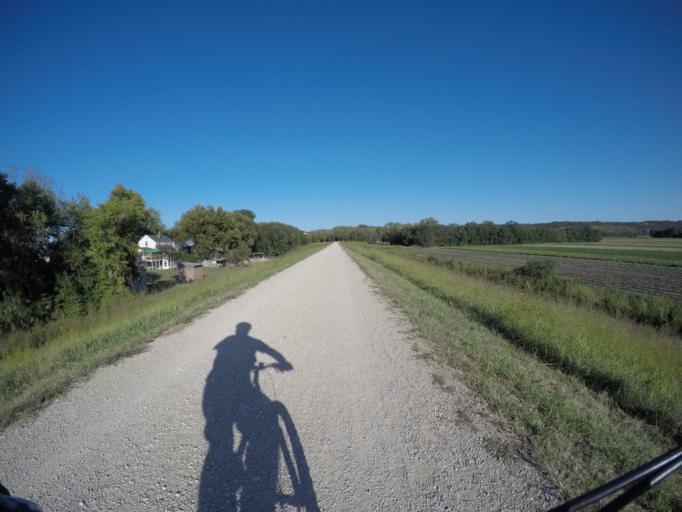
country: US
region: Kansas
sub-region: Riley County
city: Manhattan
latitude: 39.1708
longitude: -96.5664
